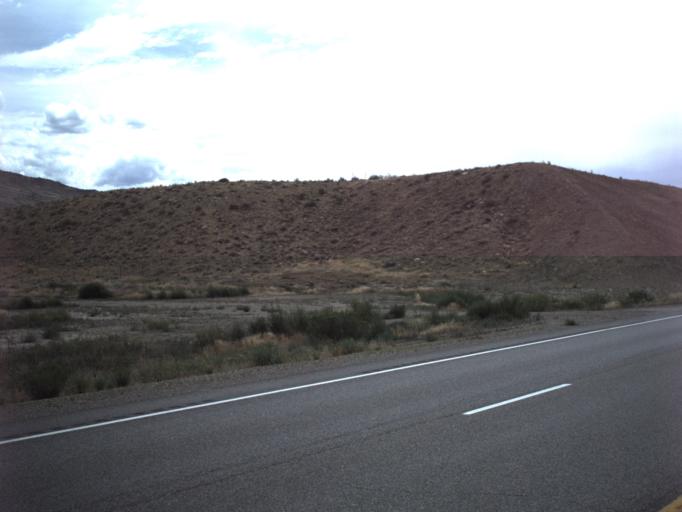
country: US
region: Utah
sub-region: Carbon County
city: East Carbon City
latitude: 39.2868
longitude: -110.3513
